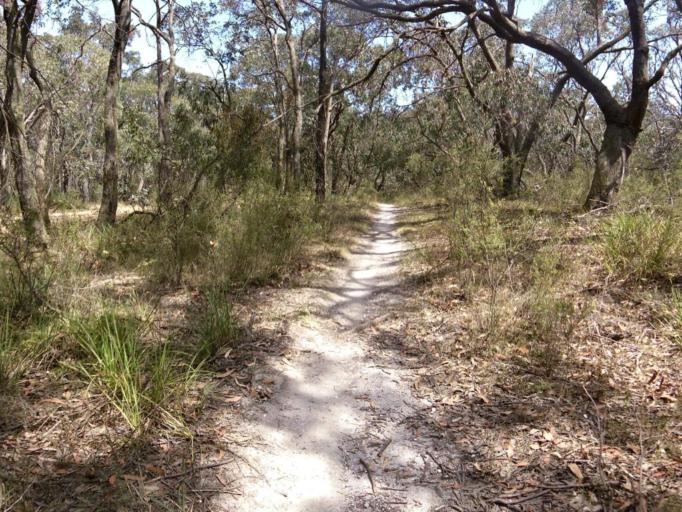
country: AU
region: Victoria
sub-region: Melton
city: Melton West
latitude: -37.5020
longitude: 144.5487
